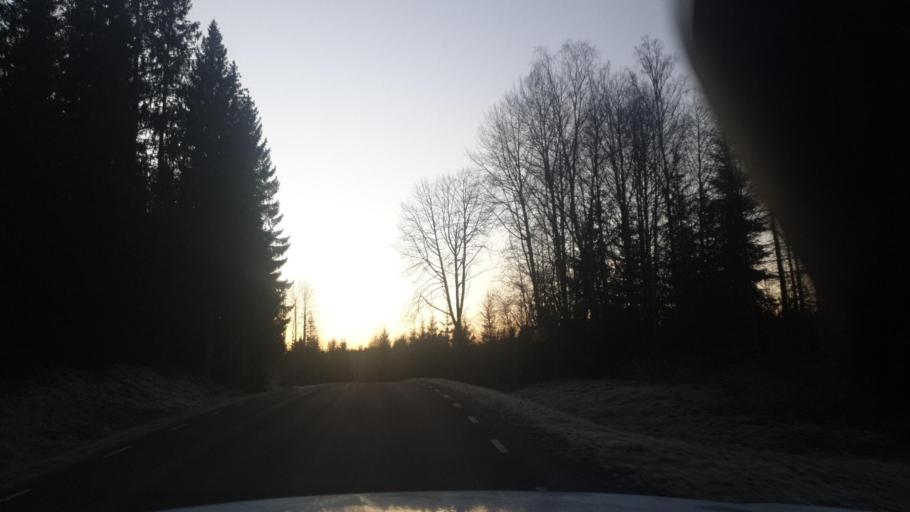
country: SE
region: Vaermland
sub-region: Eda Kommun
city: Charlottenberg
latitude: 59.9239
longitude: 12.3153
